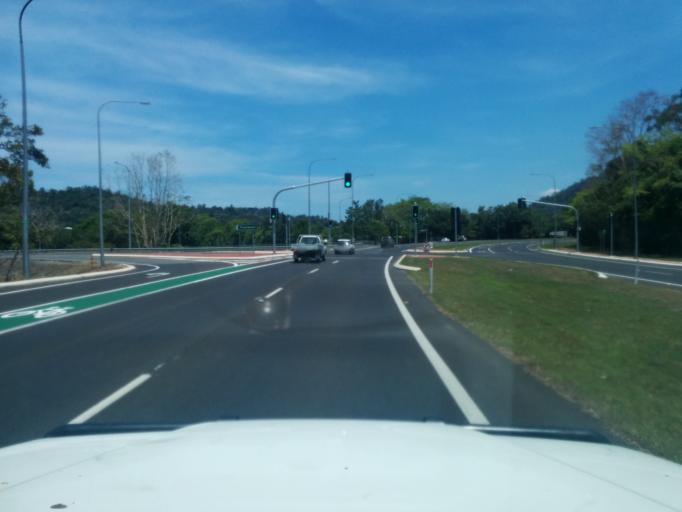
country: AU
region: Queensland
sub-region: Cairns
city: Redlynch
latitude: -16.8958
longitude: 145.7088
